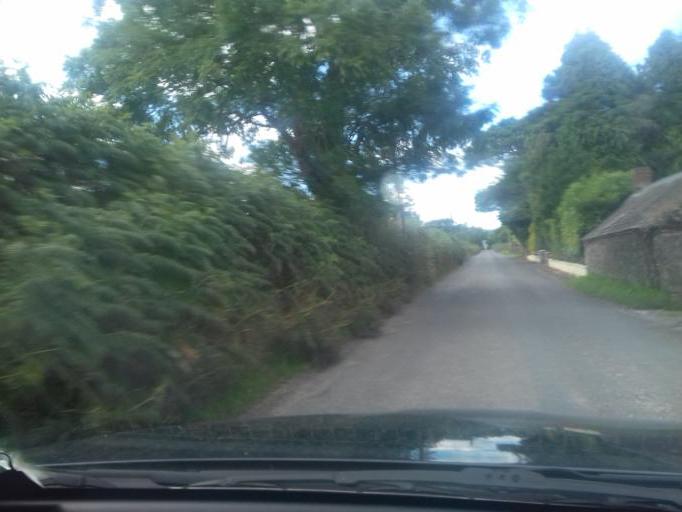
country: IE
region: Munster
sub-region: Waterford
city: Portlaw
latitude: 52.2138
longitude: -7.4336
